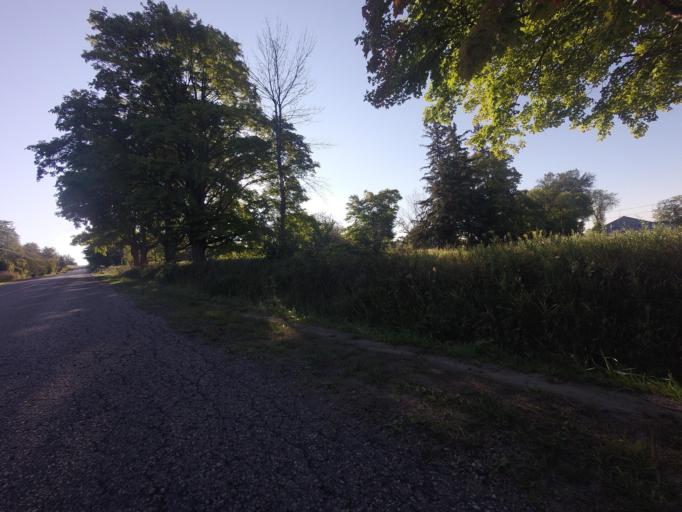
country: CA
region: Ontario
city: Bradford West Gwillimbury
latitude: 44.0402
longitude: -79.7827
